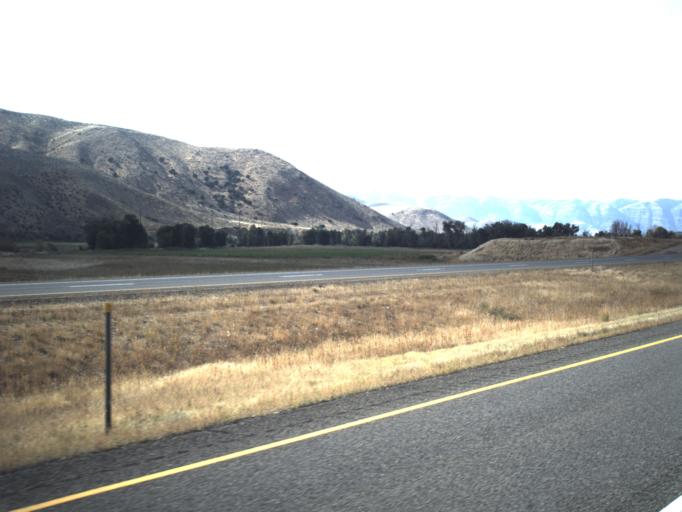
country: US
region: Utah
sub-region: Summit County
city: Coalville
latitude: 40.9842
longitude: -111.4495
